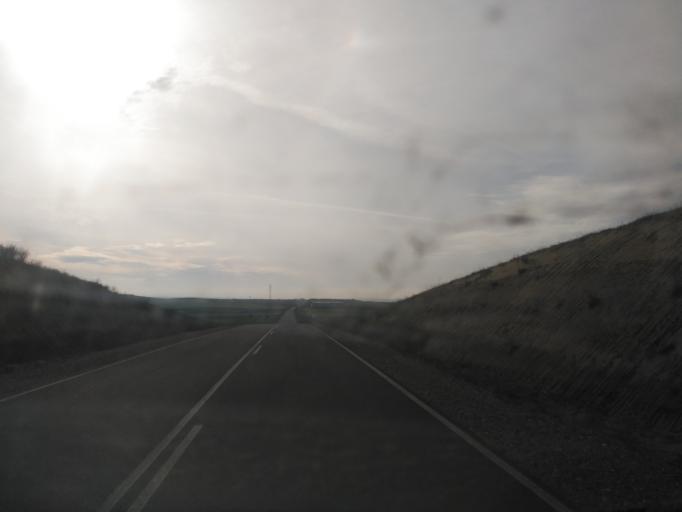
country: ES
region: Castille and Leon
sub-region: Provincia de Salamanca
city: Moriscos
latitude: 41.0006
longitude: -5.5894
